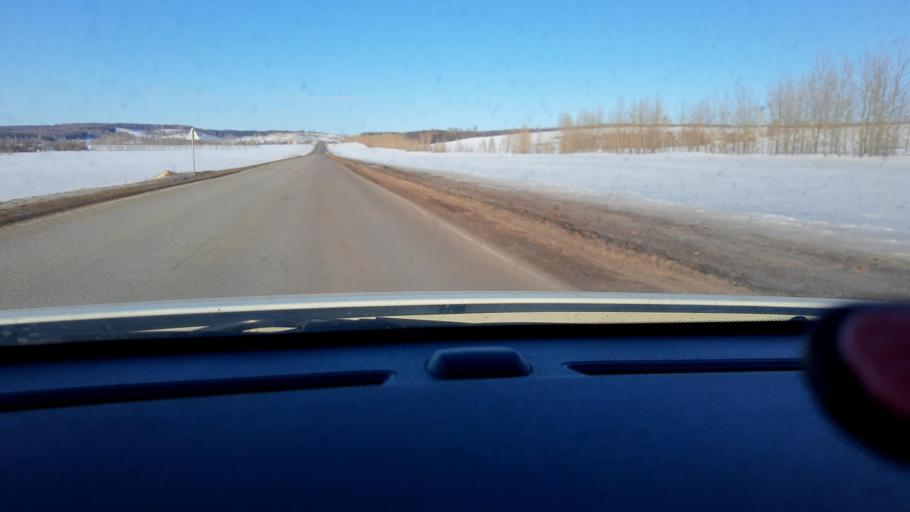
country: RU
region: Bashkortostan
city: Avdon
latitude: 54.4409
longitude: 55.8383
